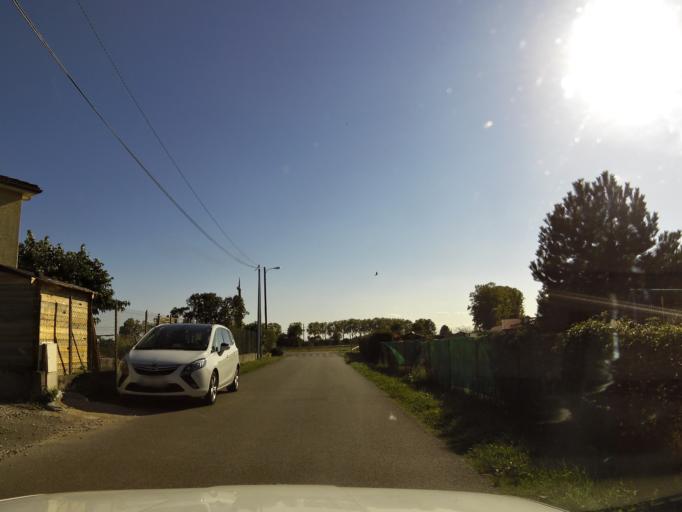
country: FR
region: Rhone-Alpes
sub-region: Departement de l'Ain
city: Meximieux
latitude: 45.9086
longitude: 5.2085
